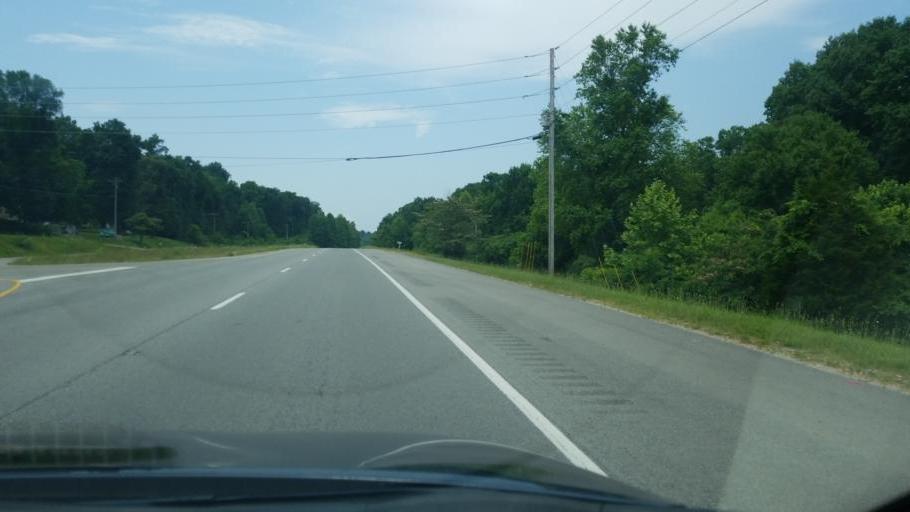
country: US
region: Tennessee
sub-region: Humphreys County
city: Johnsonville
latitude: 36.0685
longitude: -87.8785
